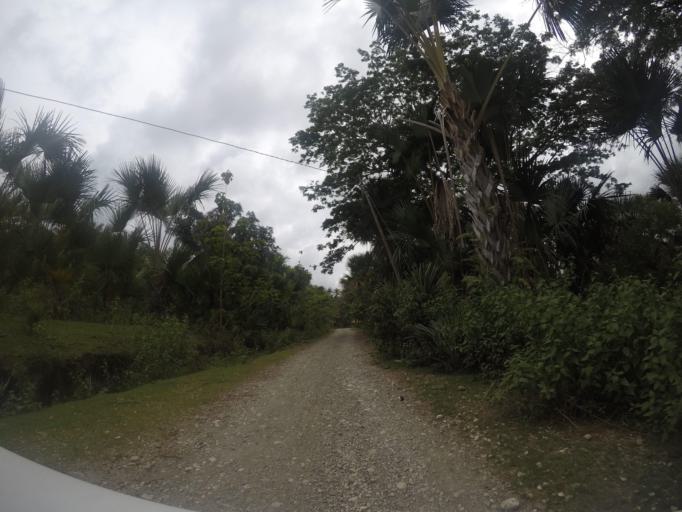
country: TL
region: Viqueque
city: Viqueque
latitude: -8.8547
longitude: 126.3677
